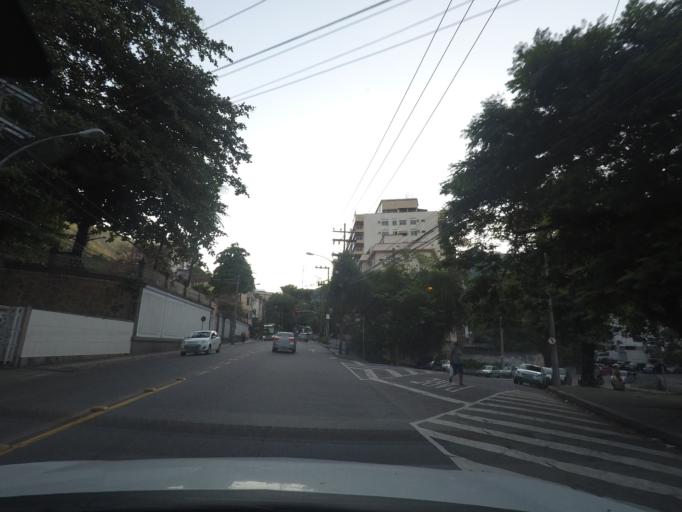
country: BR
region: Rio de Janeiro
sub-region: Rio De Janeiro
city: Rio de Janeiro
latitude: -22.9398
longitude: -43.2488
